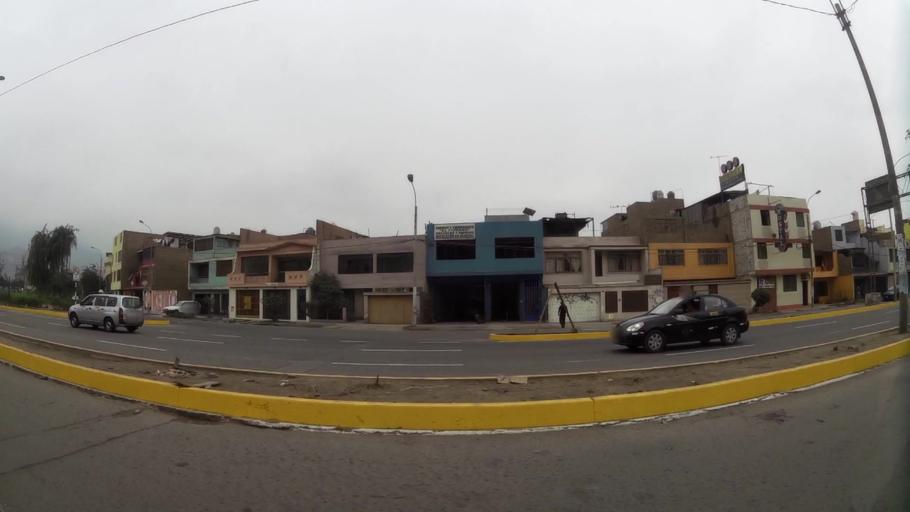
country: PE
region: Lima
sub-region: Lima
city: Independencia
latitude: -11.9779
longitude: -77.0685
